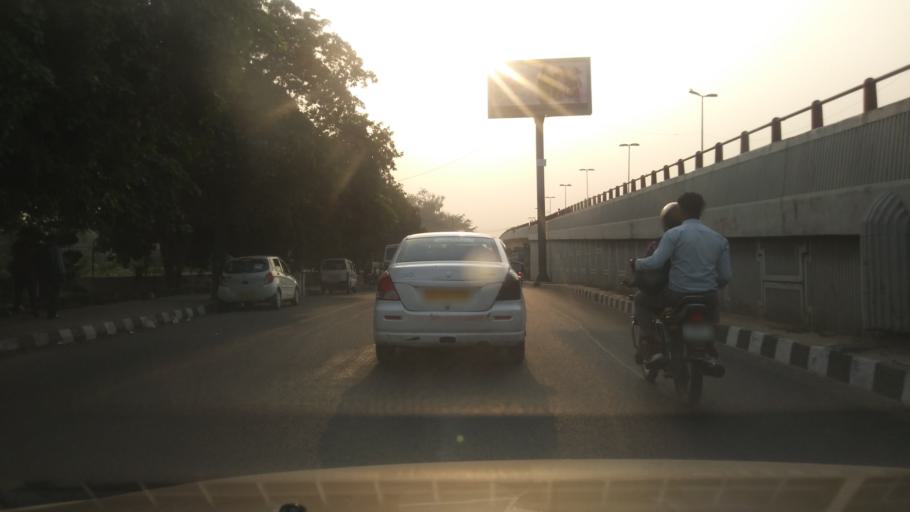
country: IN
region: Uttar Pradesh
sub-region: Gautam Buddha Nagar
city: Noida
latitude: 28.5465
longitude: 77.2521
